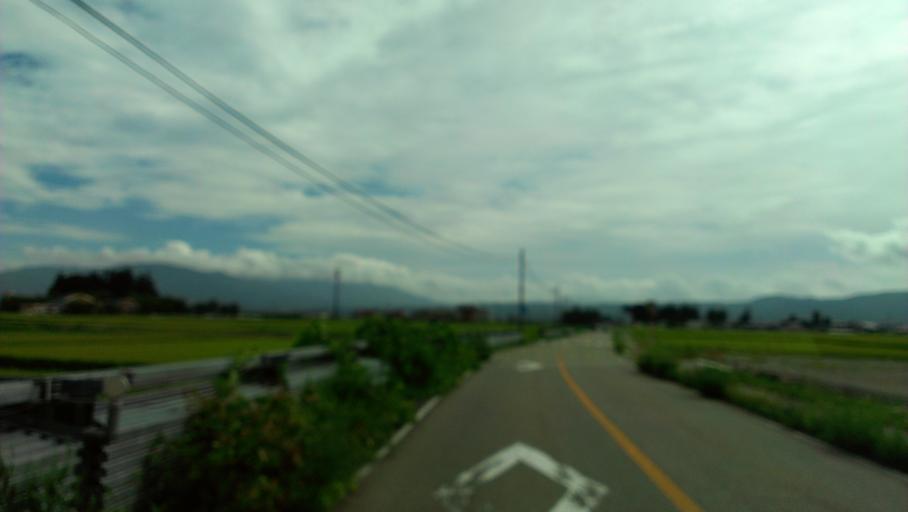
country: JP
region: Fukushima
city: Kitakata
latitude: 37.4949
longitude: 139.8655
